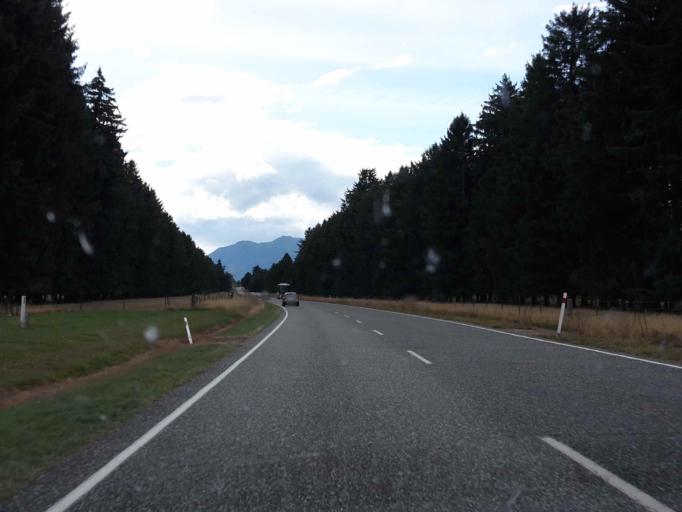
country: NZ
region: Otago
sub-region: Queenstown-Lakes District
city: Wanaka
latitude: -44.7301
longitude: 169.1368
